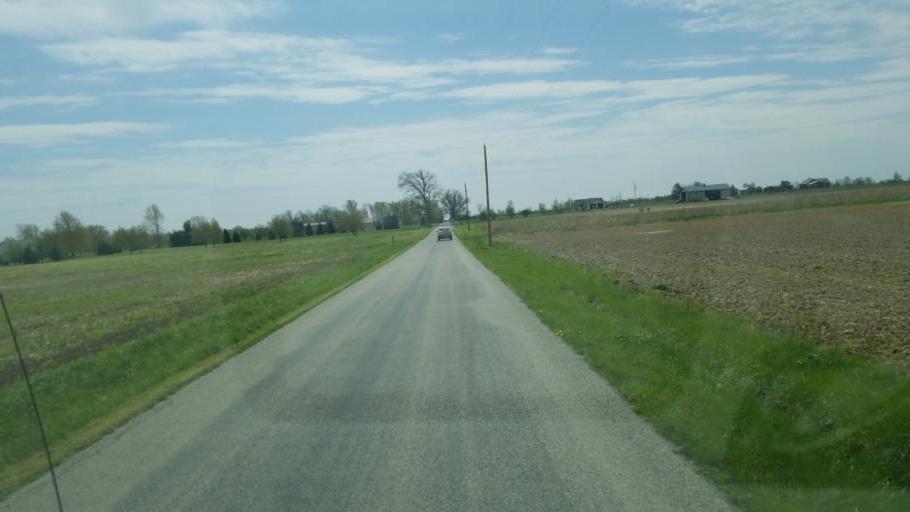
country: US
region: Ohio
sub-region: Allen County
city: Bluffton
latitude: 40.8064
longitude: -83.9092
